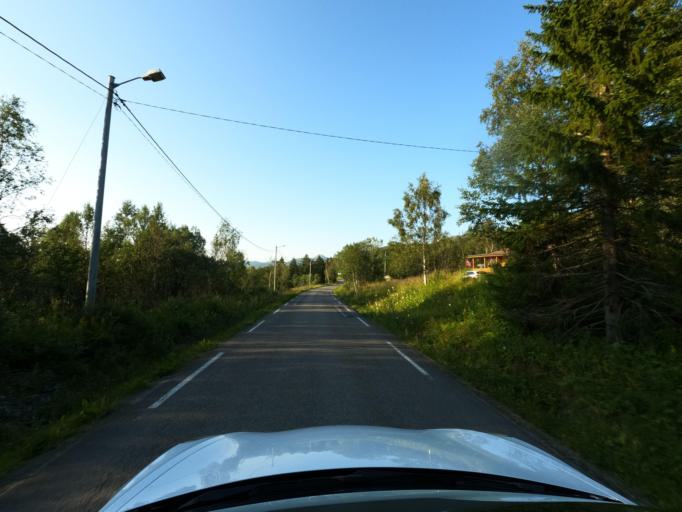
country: NO
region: Nordland
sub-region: Ballangen
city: Ballangen
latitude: 68.4957
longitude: 16.7348
